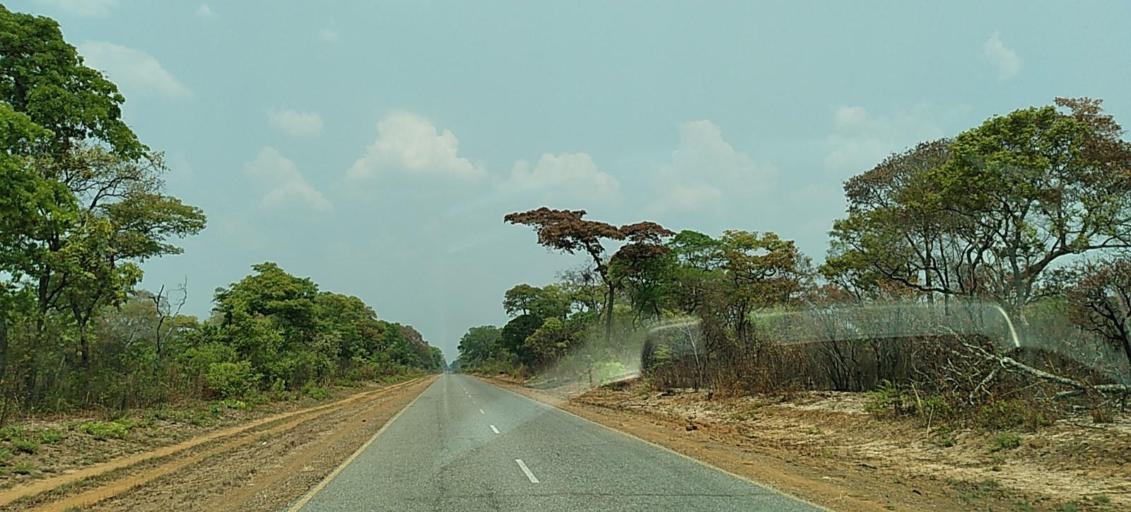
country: ZM
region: North-Western
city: Zambezi
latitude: -13.5614
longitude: 23.2144
